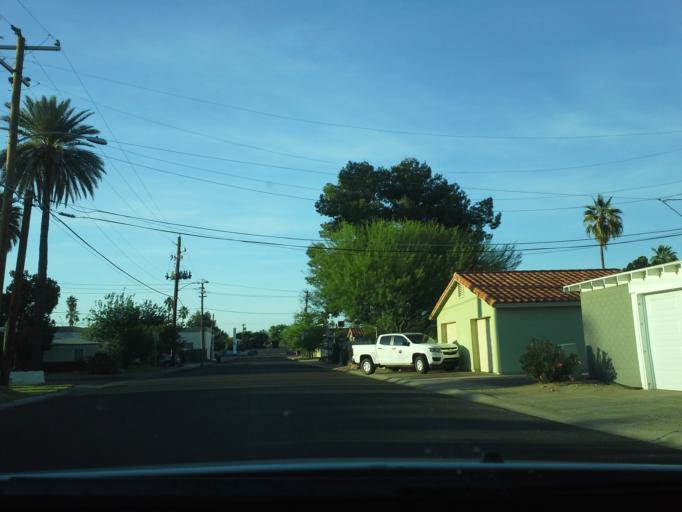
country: US
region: Arizona
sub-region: Maricopa County
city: Phoenix
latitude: 33.5078
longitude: -112.0694
